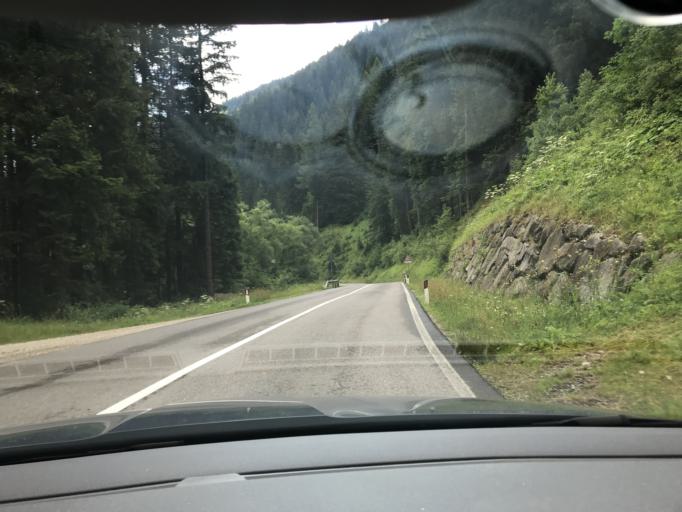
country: IT
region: Trentino-Alto Adige
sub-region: Bolzano
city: Badia
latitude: 46.6318
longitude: 11.8953
